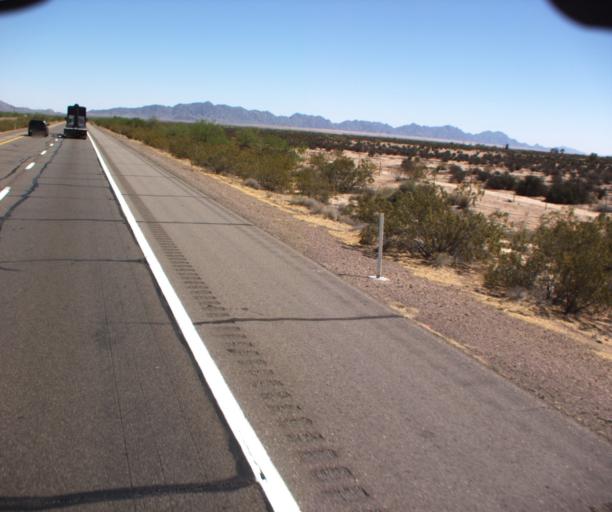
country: US
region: Arizona
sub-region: Yuma County
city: Wellton
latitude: 32.7013
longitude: -113.9009
